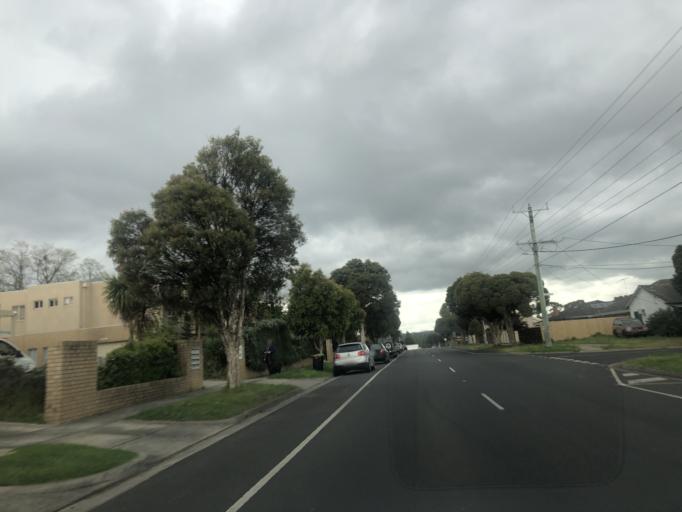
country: AU
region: Victoria
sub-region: Greater Dandenong
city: Dandenong North
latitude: -37.9637
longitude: 145.2214
